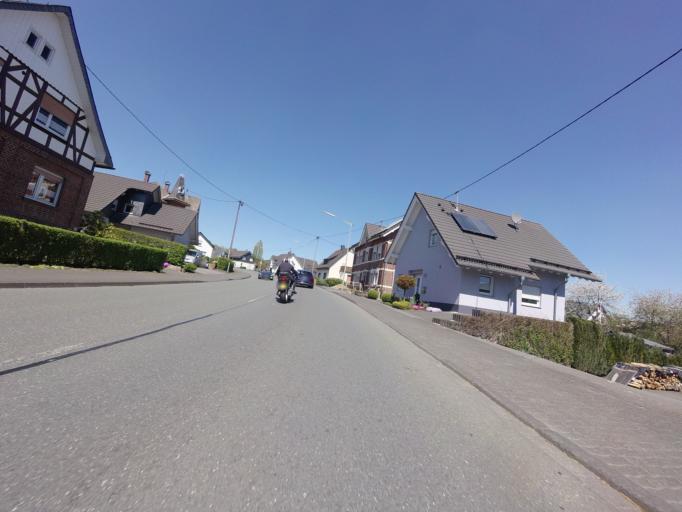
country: DE
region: North Rhine-Westphalia
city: Kreuztal
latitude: 50.9960
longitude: 7.9571
